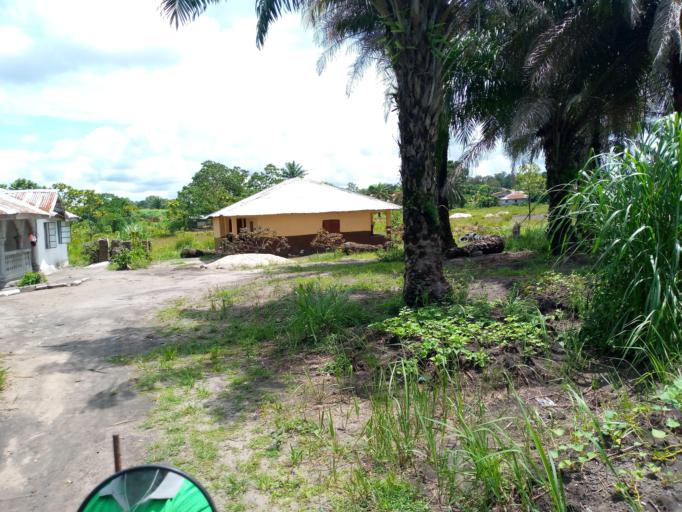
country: SL
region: Northern Province
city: Magburaka
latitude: 8.7205
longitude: -11.9258
